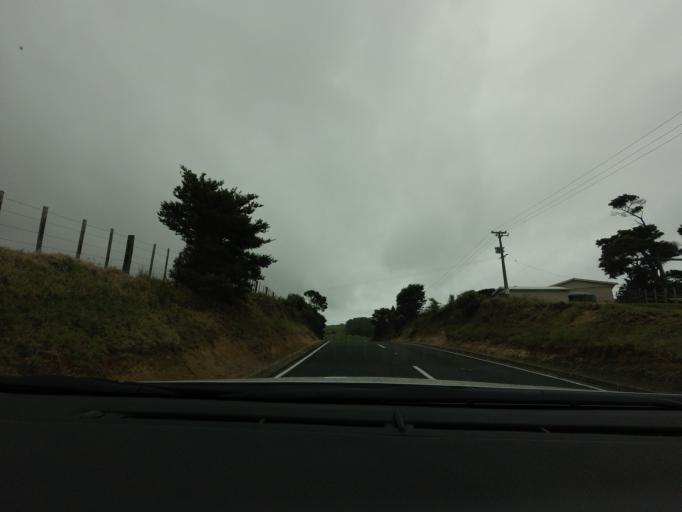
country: NZ
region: Auckland
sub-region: Auckland
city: Warkworth
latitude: -36.2866
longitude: 174.7967
